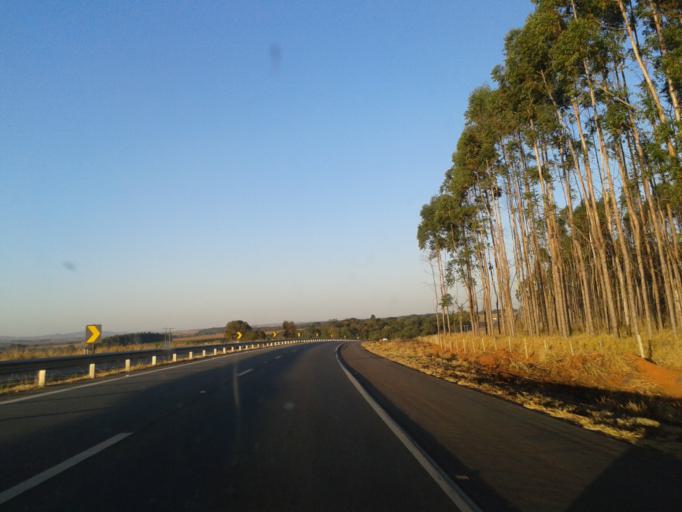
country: BR
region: Goias
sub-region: Itaberai
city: Itaberai
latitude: -16.0076
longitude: -49.9600
